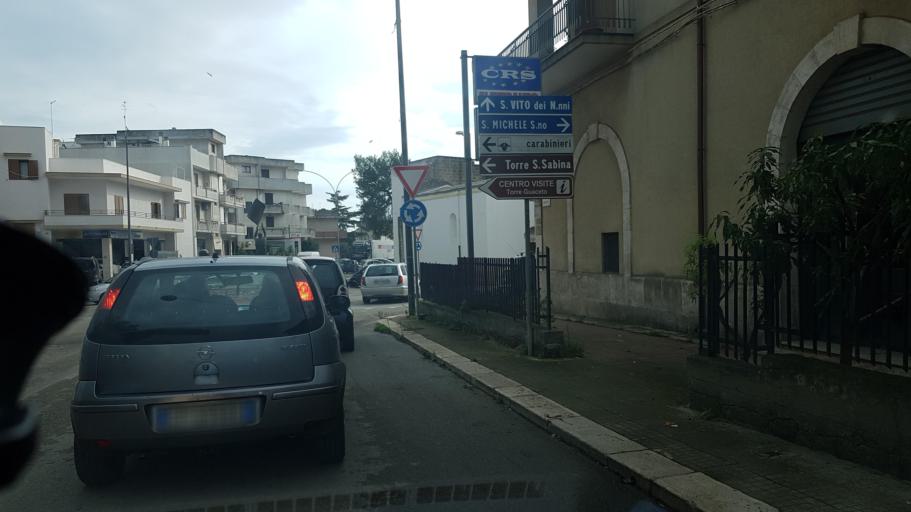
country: IT
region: Apulia
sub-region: Provincia di Brindisi
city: Carovigno
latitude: 40.7023
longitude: 17.6614
